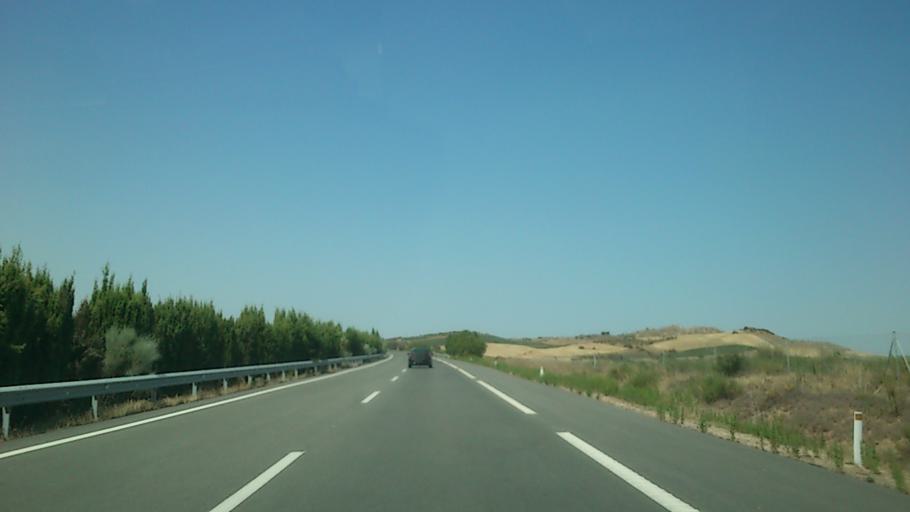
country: ES
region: Navarre
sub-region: Provincia de Navarra
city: Sartaguda
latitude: 42.3697
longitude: -2.0777
